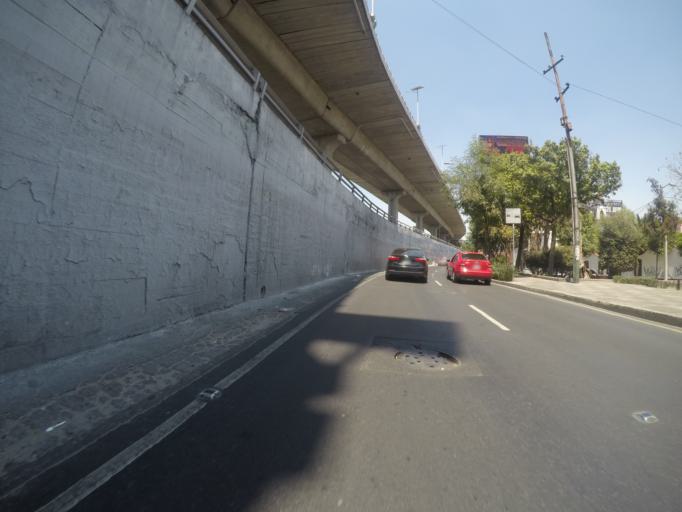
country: MX
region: Mexico City
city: Polanco
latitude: 19.4013
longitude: -99.1921
